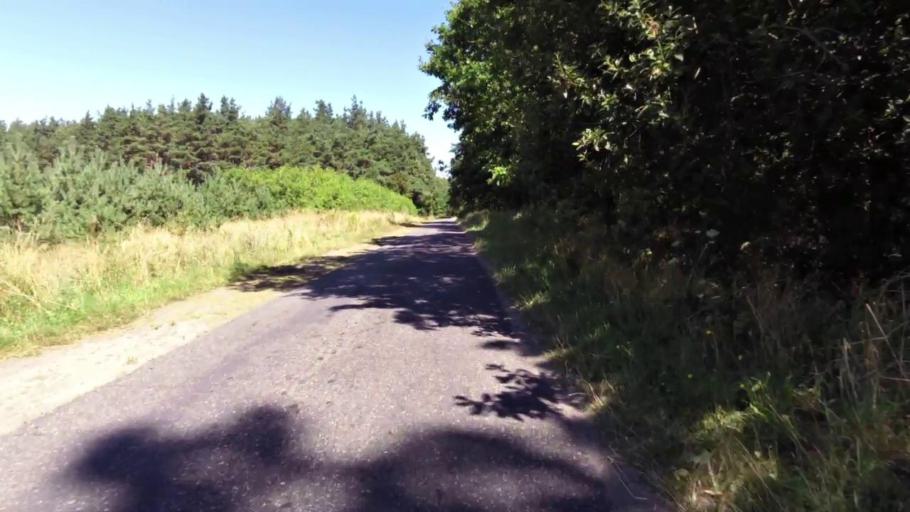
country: PL
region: West Pomeranian Voivodeship
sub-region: Powiat szczecinecki
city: Szczecinek
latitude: 53.6448
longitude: 16.7169
